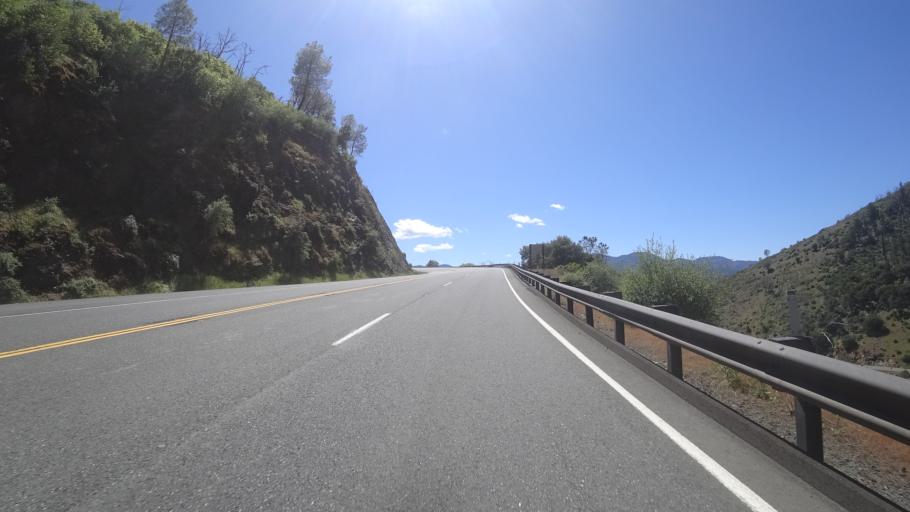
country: US
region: California
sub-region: Trinity County
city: Weaverville
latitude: 40.7396
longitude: -122.9996
